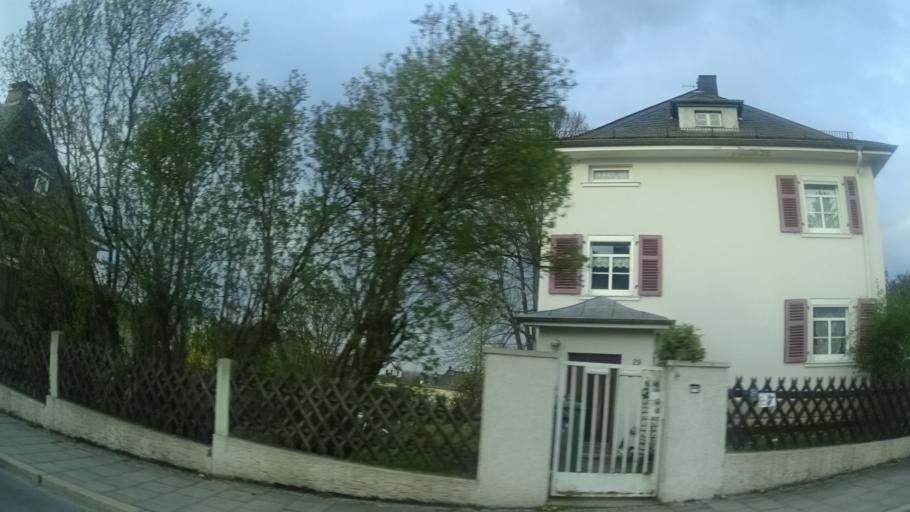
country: DE
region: Bavaria
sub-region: Upper Franconia
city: Hof
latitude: 50.3091
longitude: 11.9068
